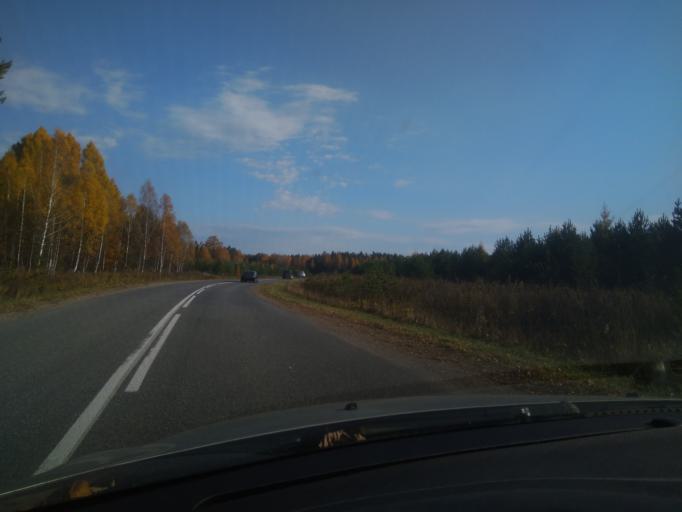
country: RU
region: Sverdlovsk
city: Mikhaylovsk
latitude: 56.5325
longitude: 59.2115
